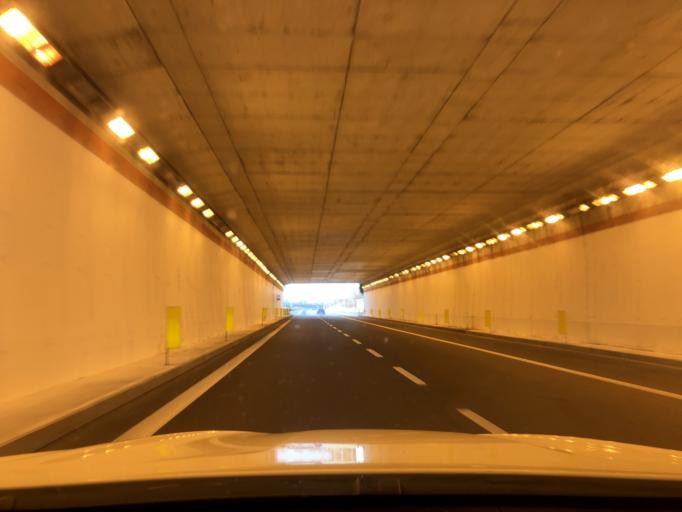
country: IT
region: Lombardy
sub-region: Citta metropolitana di Milano
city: Buscate
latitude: 45.5274
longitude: 8.8101
